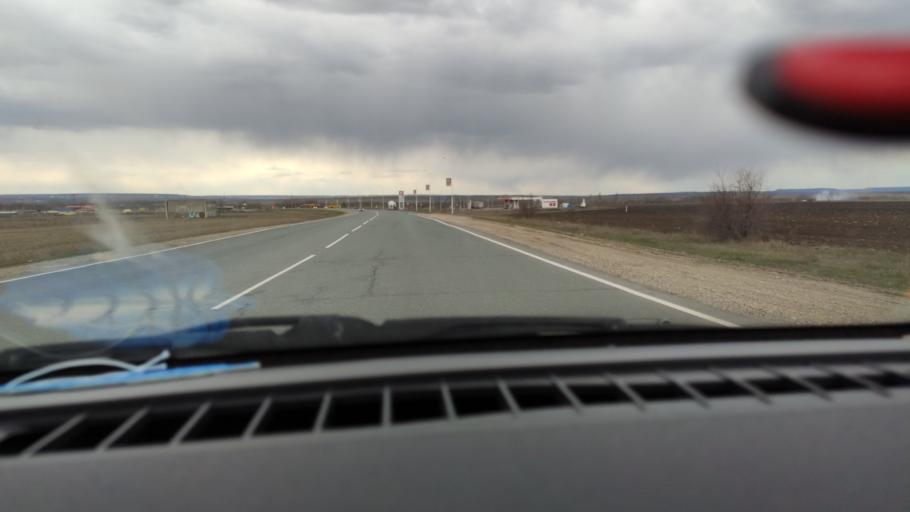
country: RU
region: Saratov
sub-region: Saratovskiy Rayon
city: Saratov
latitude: 51.7346
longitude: 46.0360
